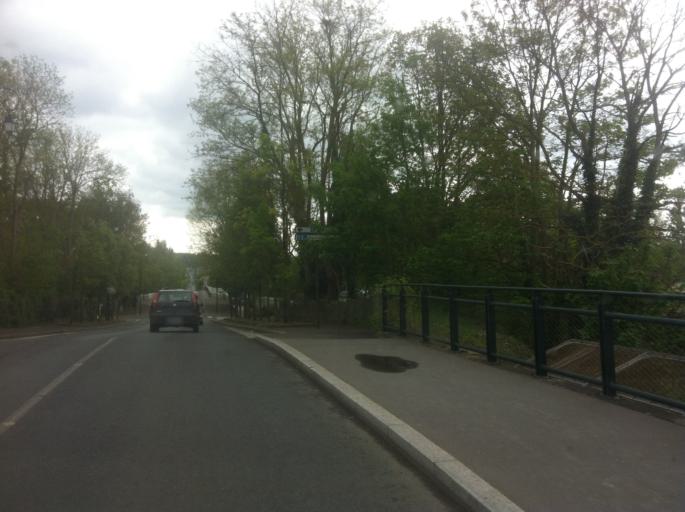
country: FR
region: Ile-de-France
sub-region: Departement du Val-d'Oise
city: Auvers-sur-Oise
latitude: 49.0711
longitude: 2.1772
